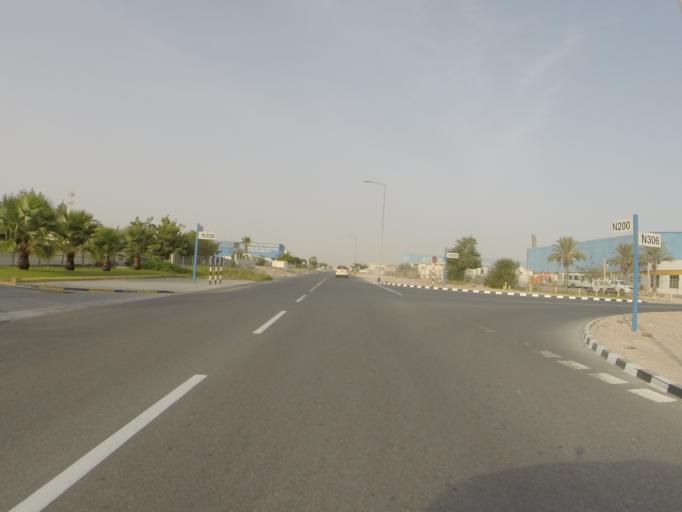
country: AE
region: Dubai
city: Dubai
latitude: 24.9631
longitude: 55.0729
